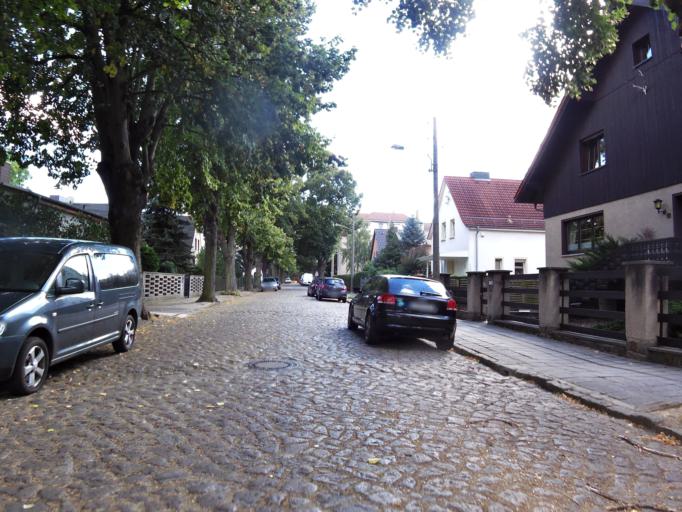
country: DE
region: Saxony
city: Leipzig
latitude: 51.3563
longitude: 12.2951
